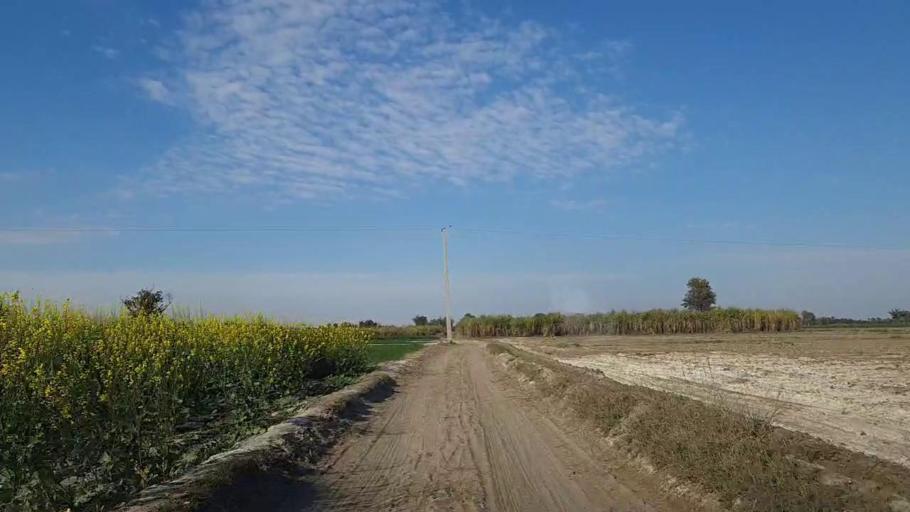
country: PK
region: Sindh
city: Khadro
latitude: 26.3093
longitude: 68.8343
